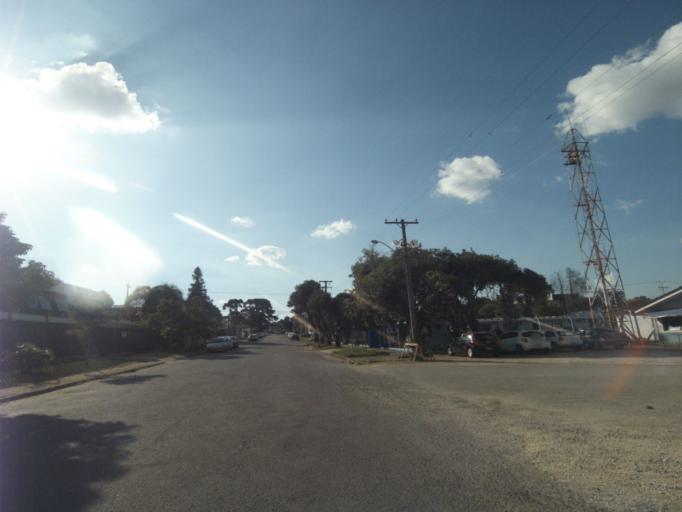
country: BR
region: Parana
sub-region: Curitiba
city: Curitiba
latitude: -25.4596
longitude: -49.2536
